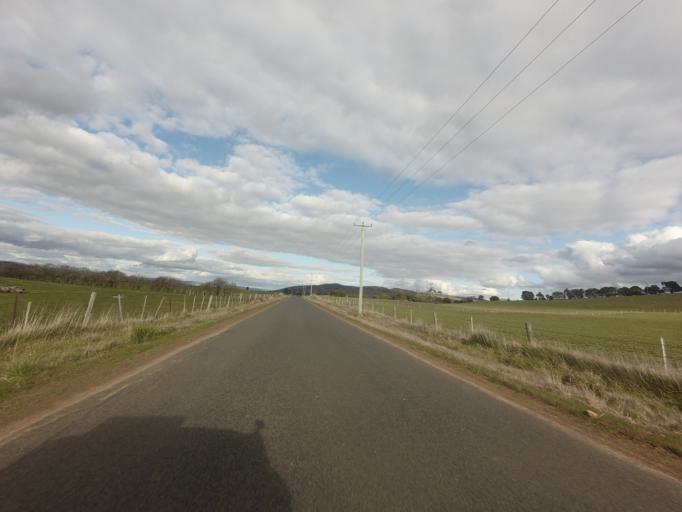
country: AU
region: Tasmania
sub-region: Northern Midlands
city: Evandale
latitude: -41.8971
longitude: 147.3430
